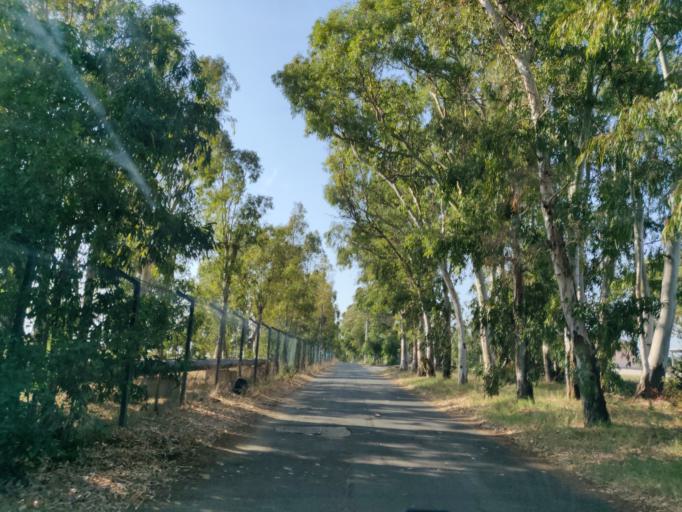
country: IT
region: Latium
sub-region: Citta metropolitana di Roma Capitale
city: Aurelia
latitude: 42.1321
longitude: 11.7648
